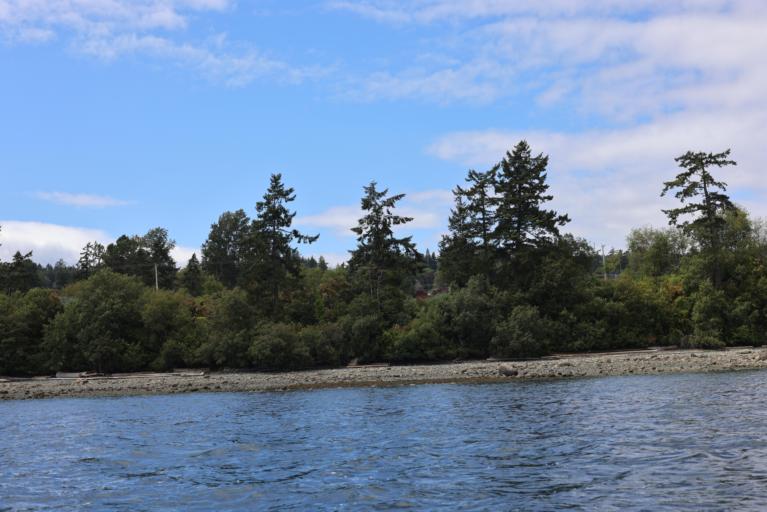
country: CA
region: British Columbia
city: North Saanich
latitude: 48.6207
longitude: -123.4028
